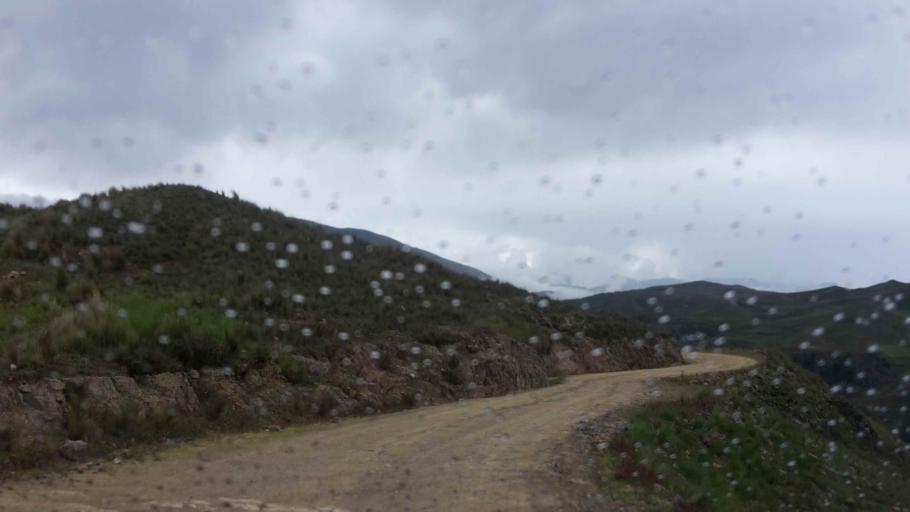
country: BO
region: Cochabamba
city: Cochabamba
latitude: -17.1442
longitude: -66.1032
